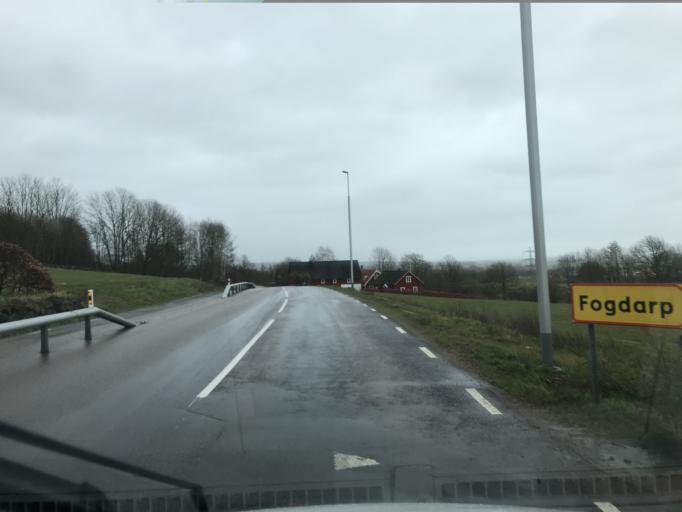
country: SE
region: Skane
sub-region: Bastads Kommun
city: Forslov
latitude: 56.3497
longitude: 12.8512
